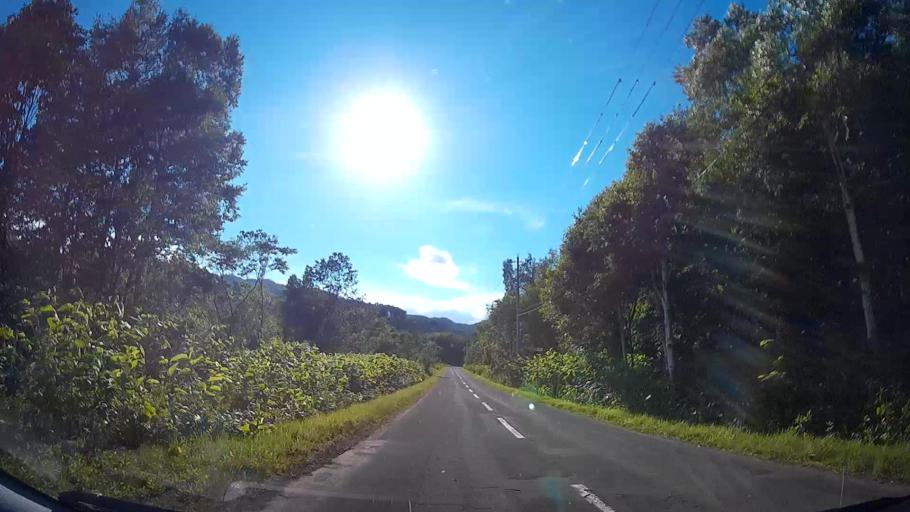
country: JP
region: Hokkaido
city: Sapporo
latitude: 42.9818
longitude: 141.1315
